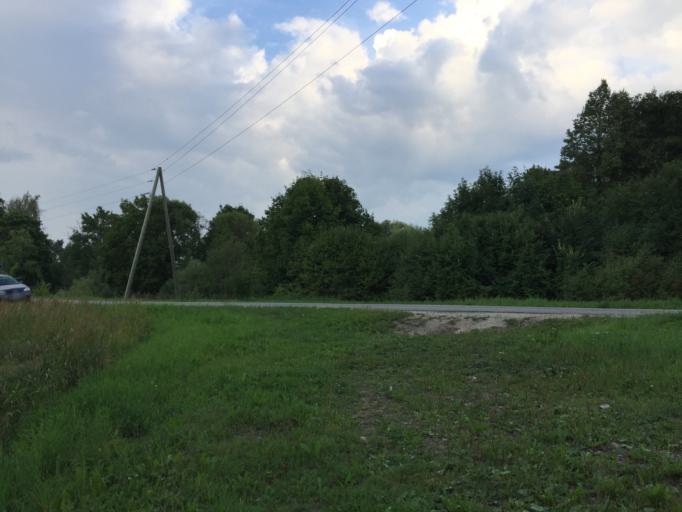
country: LV
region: Dobeles Rajons
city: Dobele
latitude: 56.6001
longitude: 23.3066
